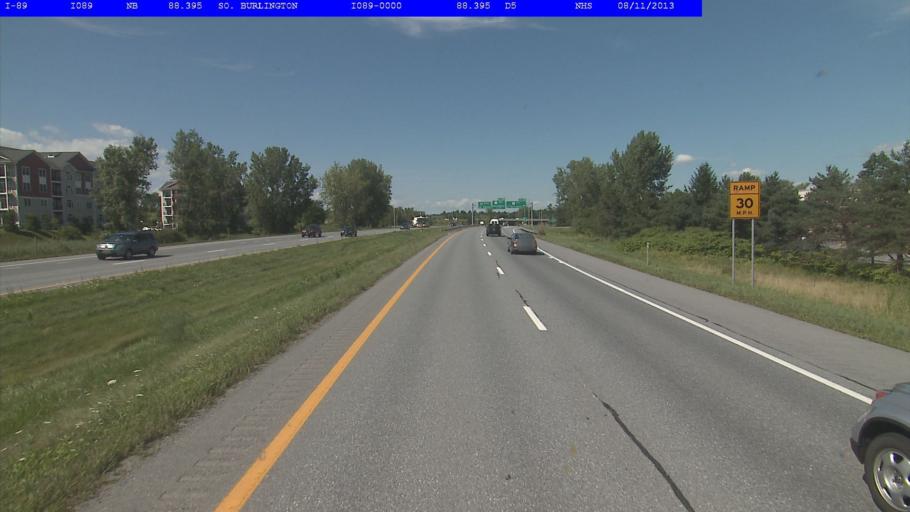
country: US
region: Vermont
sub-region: Chittenden County
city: South Burlington
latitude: 44.4653
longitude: -73.1855
